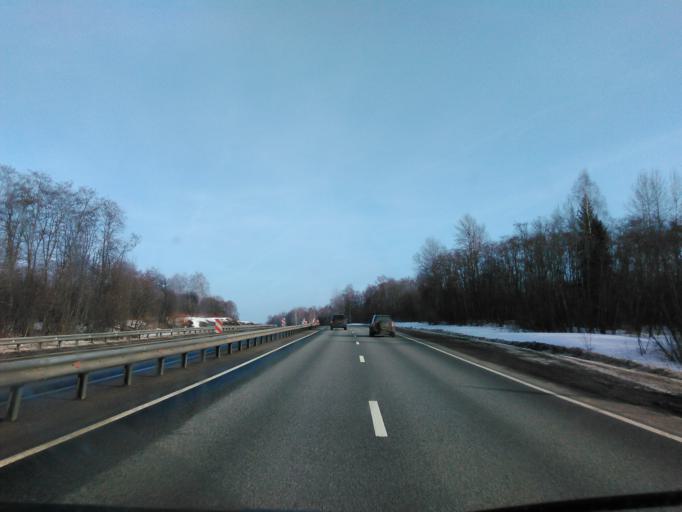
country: RU
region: Smolensk
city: Vyaz'ma
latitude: 55.1917
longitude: 33.9527
